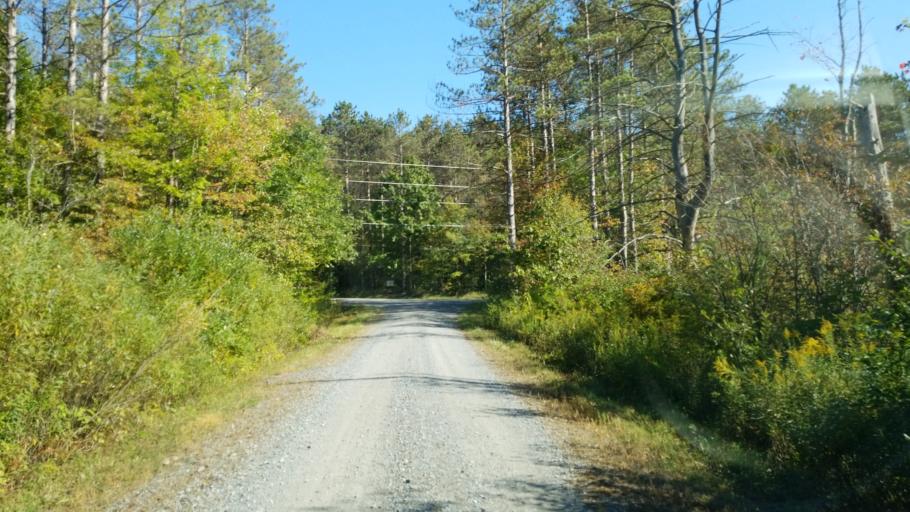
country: US
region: Pennsylvania
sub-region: Clearfield County
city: Treasure Lake
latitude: 41.1473
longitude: -78.5727
